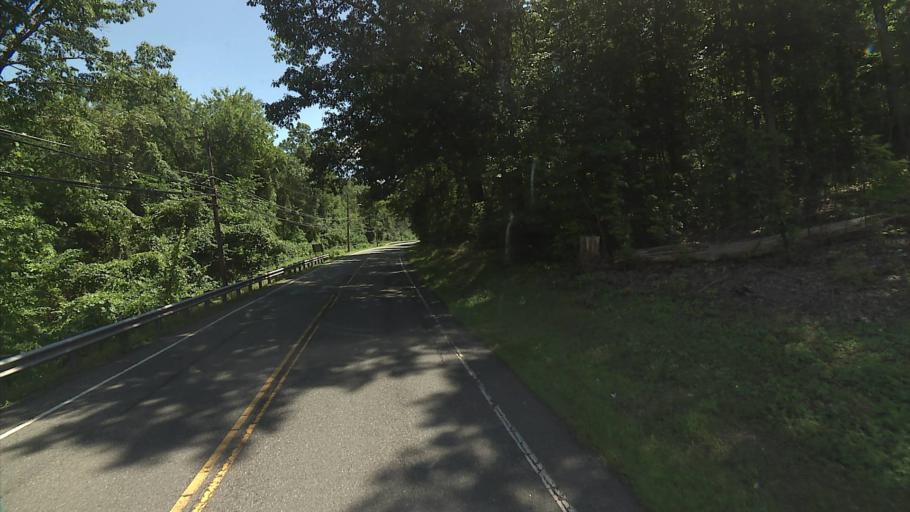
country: US
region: Massachusetts
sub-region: Hampden County
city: Southwick
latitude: 42.0121
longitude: -72.7260
